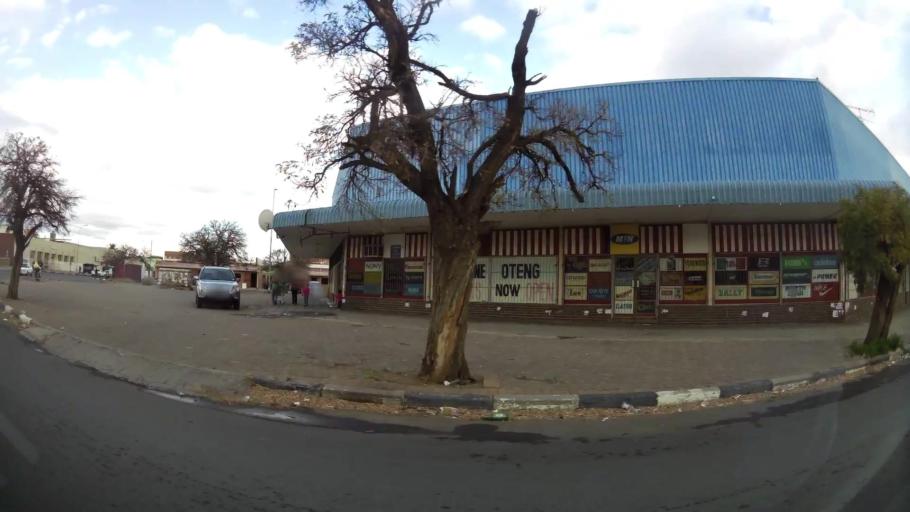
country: ZA
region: Orange Free State
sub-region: Lejweleputswa District Municipality
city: Welkom
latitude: -27.9816
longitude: 26.7330
